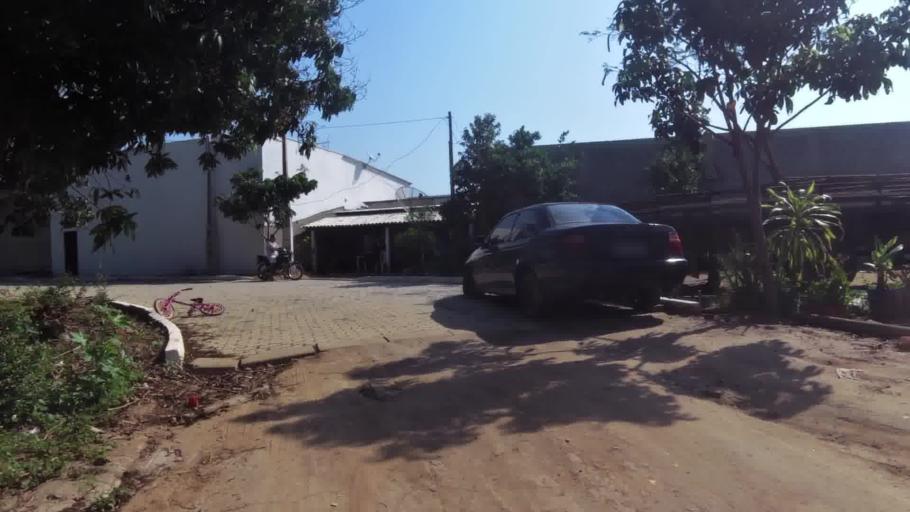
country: BR
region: Espirito Santo
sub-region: Piuma
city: Piuma
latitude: -20.8063
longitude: -40.7388
